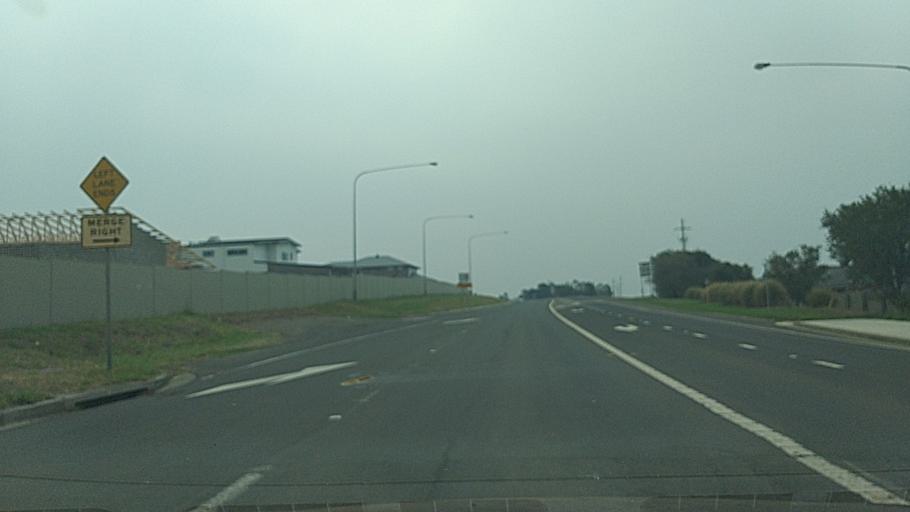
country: AU
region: New South Wales
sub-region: Shellharbour
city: Croom
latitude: -34.5937
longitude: 150.8482
